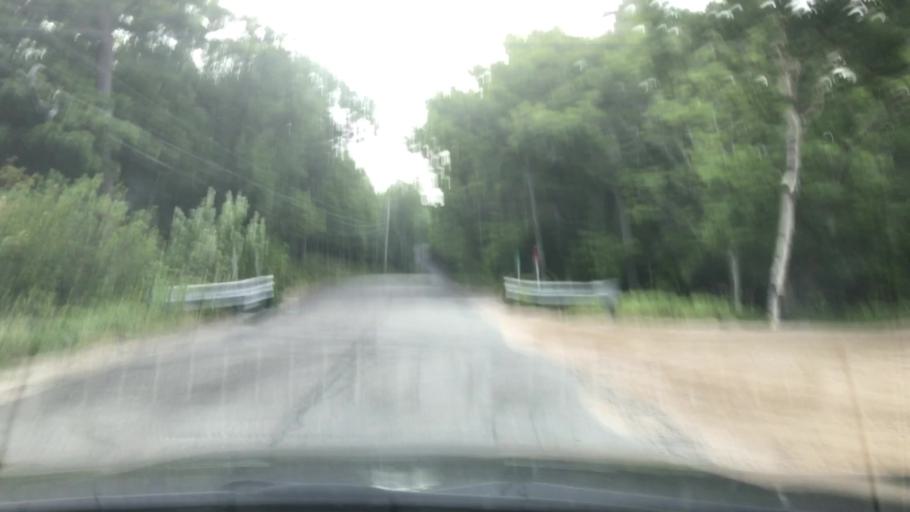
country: US
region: Maine
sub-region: Hancock County
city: Bar Harbor
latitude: 44.3556
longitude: -68.1849
